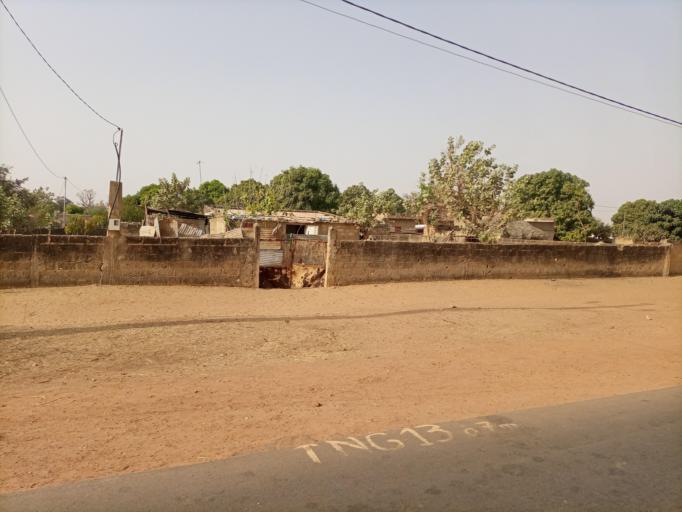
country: SN
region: Fatick
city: Foundiougne
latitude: 14.1210
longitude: -16.4389
